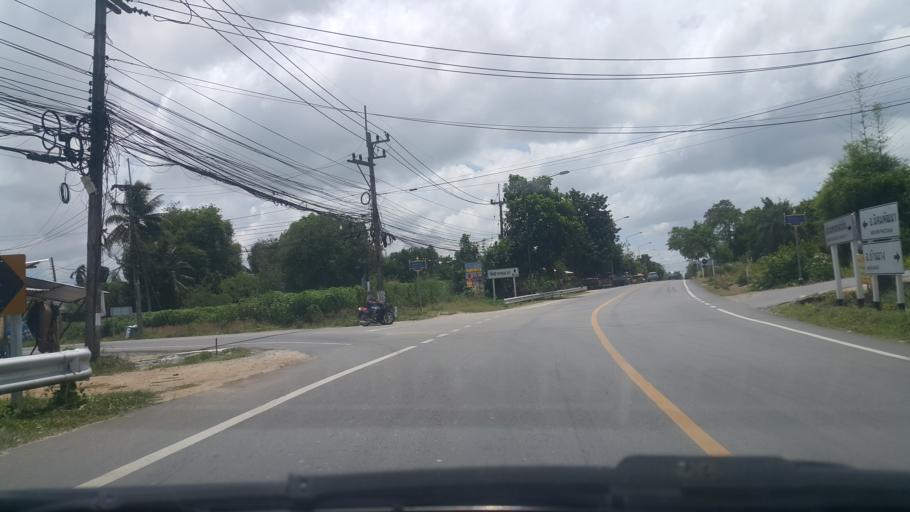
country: TH
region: Rayong
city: Ban Chang
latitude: 12.7633
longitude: 101.0187
